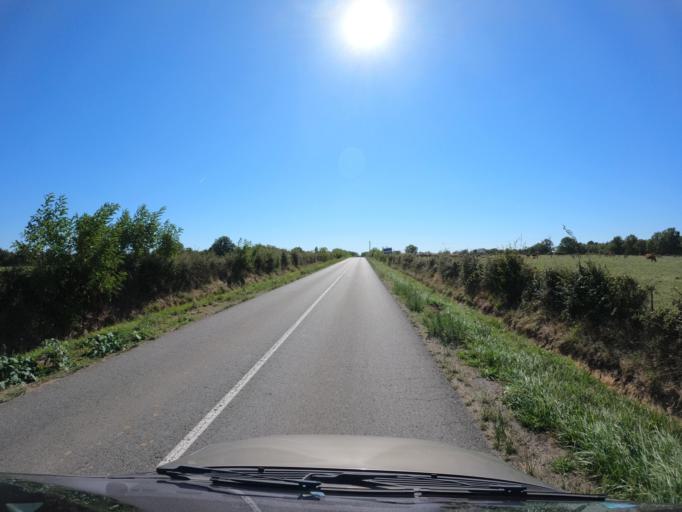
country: FR
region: Poitou-Charentes
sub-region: Departement de la Vienne
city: Lathus-Saint-Remy
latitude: 46.3473
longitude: 0.9497
